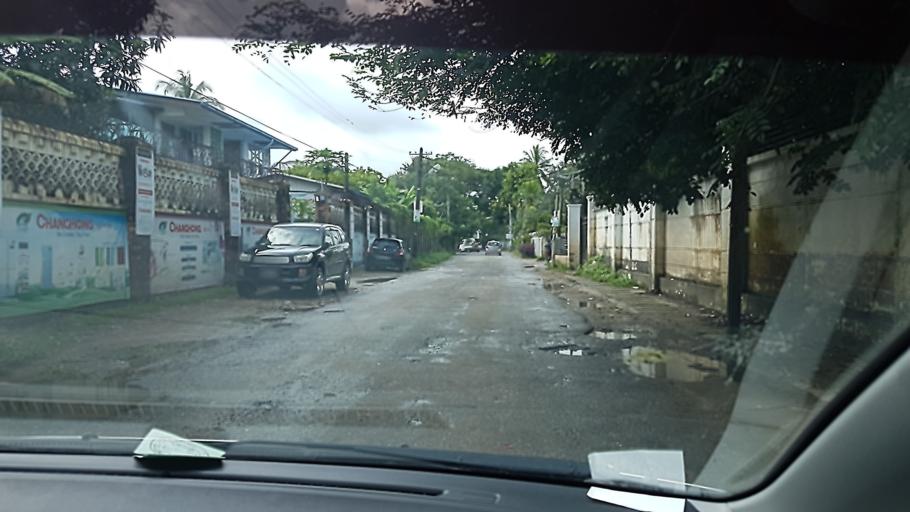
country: MM
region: Yangon
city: Yangon
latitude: 16.8177
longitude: 96.1479
